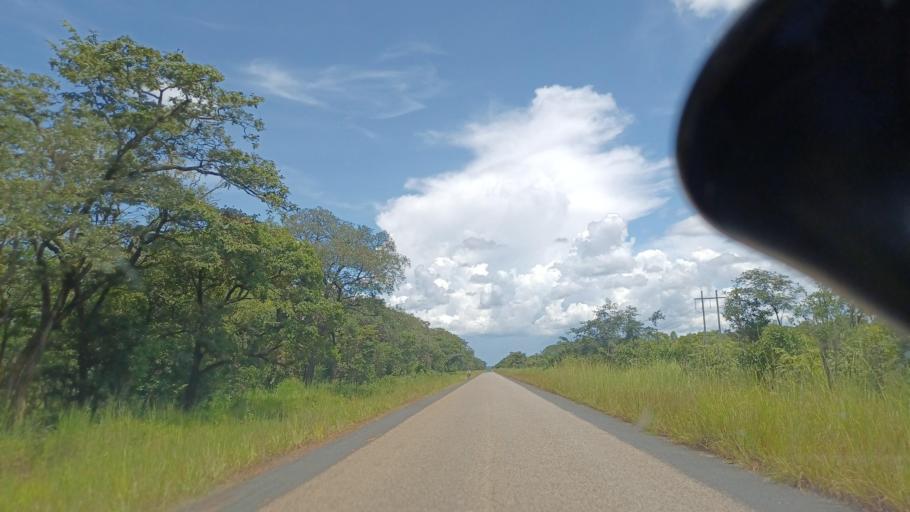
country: ZM
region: North-Western
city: Solwezi
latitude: -12.5816
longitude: 26.1303
